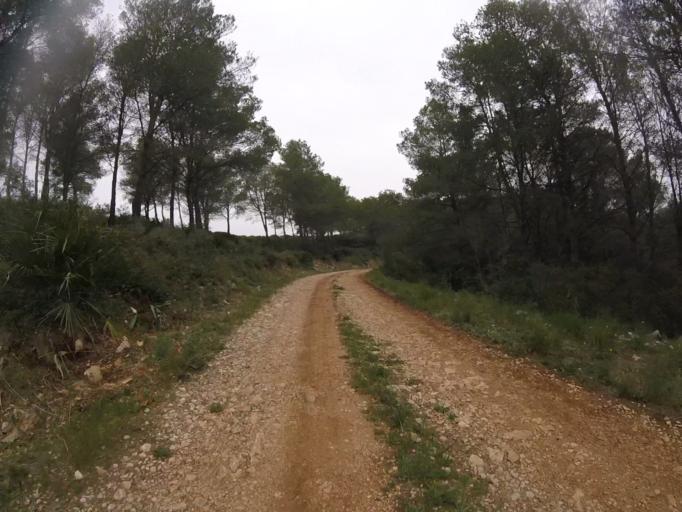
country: ES
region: Valencia
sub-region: Provincia de Castello
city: Alcala de Xivert
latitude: 40.3093
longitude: 0.2612
